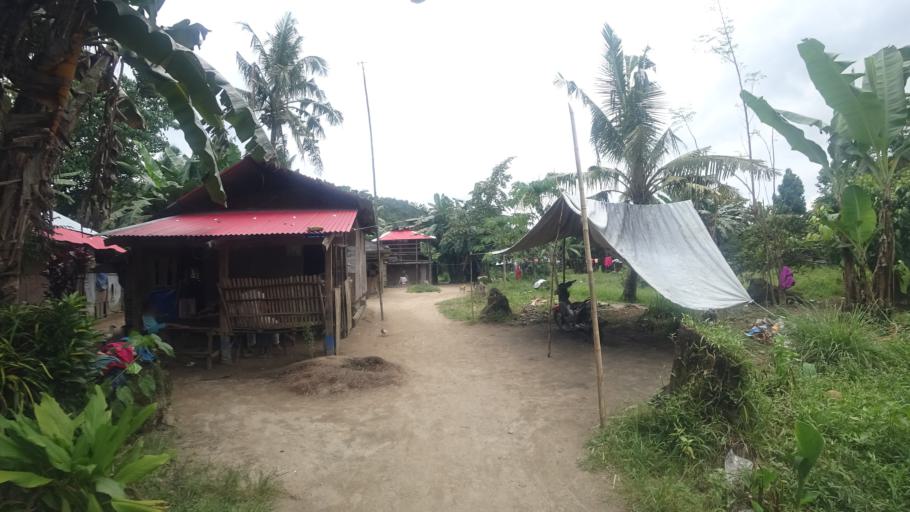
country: PH
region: Eastern Visayas
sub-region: Province of Leyte
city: Bugho
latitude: 10.8052
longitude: 124.9684
